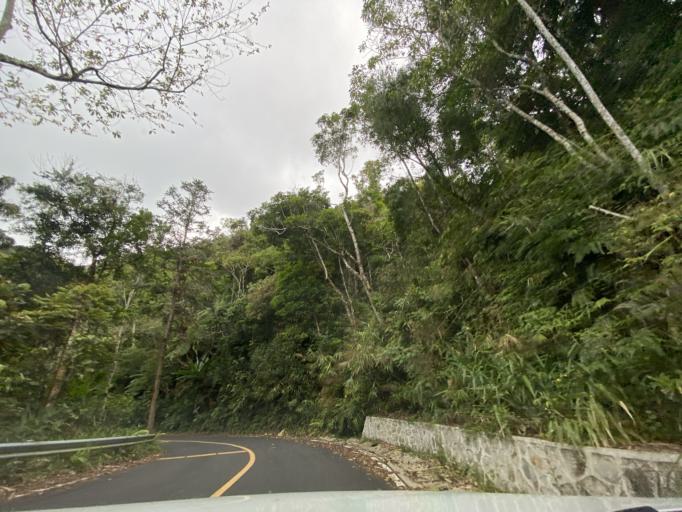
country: CN
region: Hainan
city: Diaoluoshan
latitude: 18.7144
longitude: 109.8800
